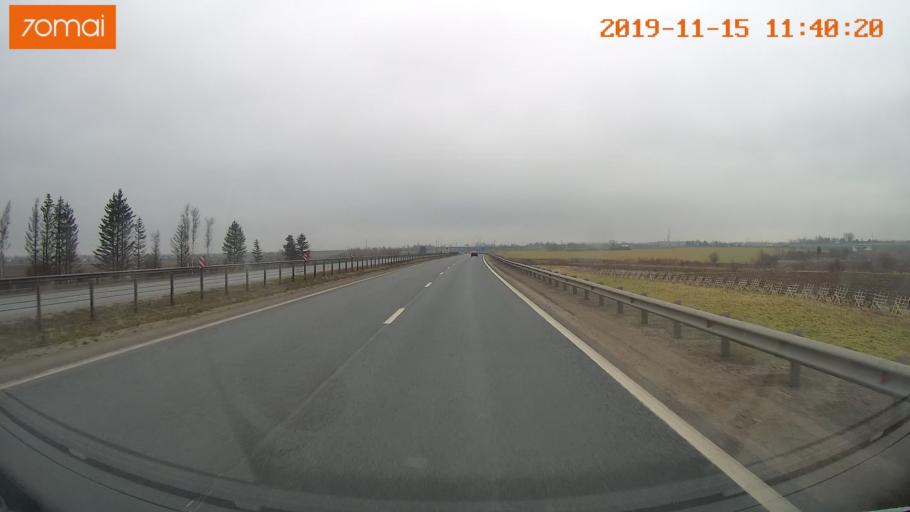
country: RU
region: Vologda
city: Molochnoye
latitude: 59.2125
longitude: 39.7488
